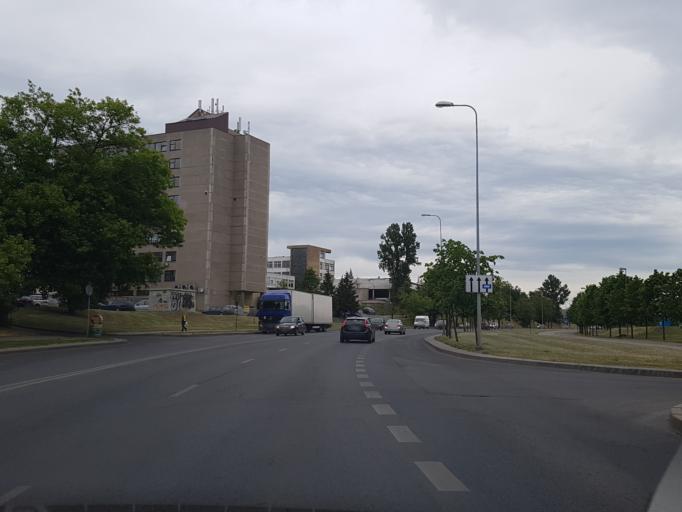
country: LT
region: Vilnius County
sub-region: Vilnius
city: Vilnius
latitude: 54.7210
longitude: 25.2858
